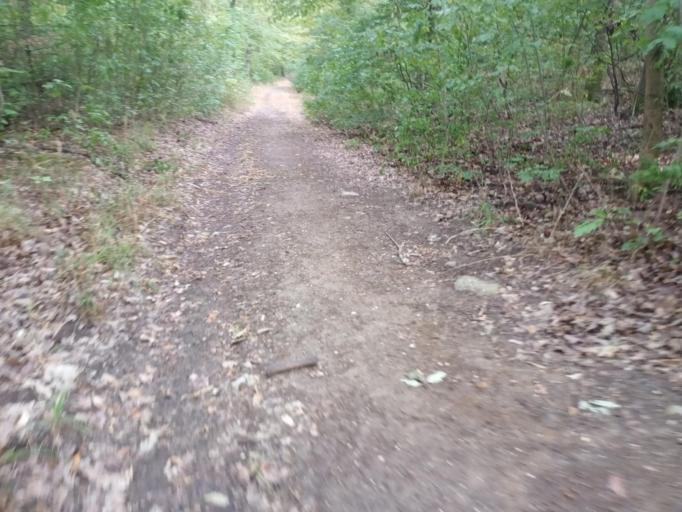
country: HU
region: Pest
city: Pilisborosjeno
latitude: 47.6216
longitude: 19.0025
